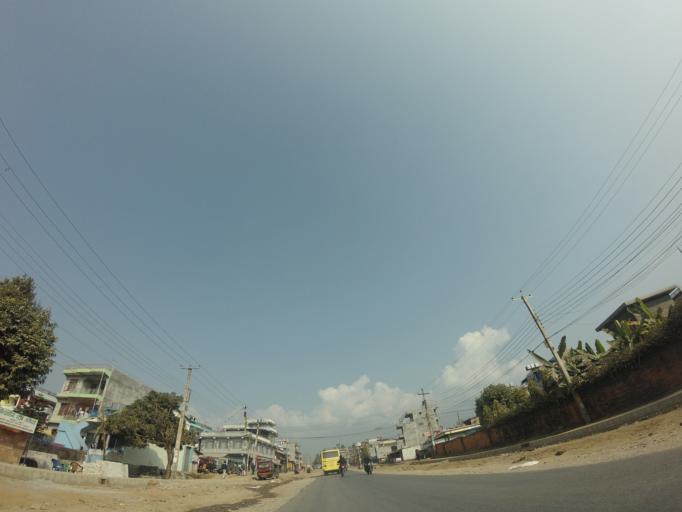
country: NP
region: Western Region
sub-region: Gandaki Zone
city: Pokhara
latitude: 28.2341
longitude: 83.9829
